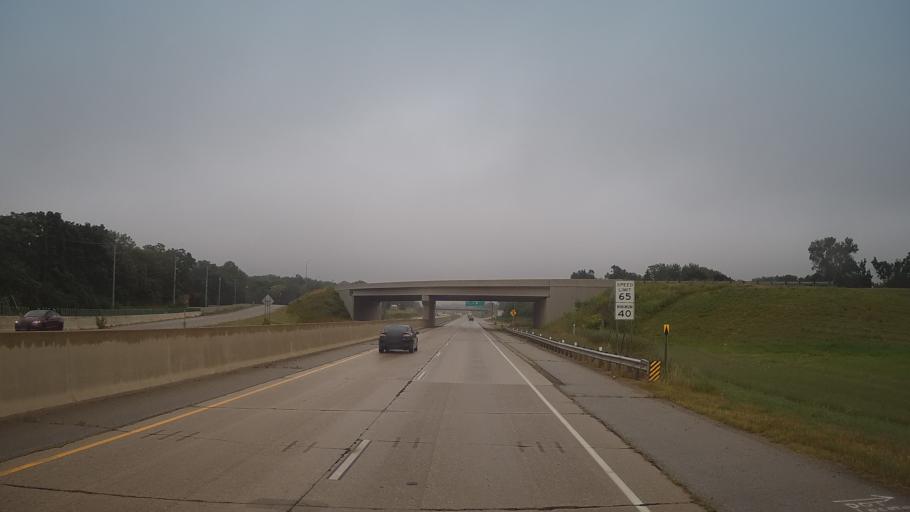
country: US
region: Minnesota
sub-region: Mower County
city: Austin
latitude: 43.6743
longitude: -92.9480
